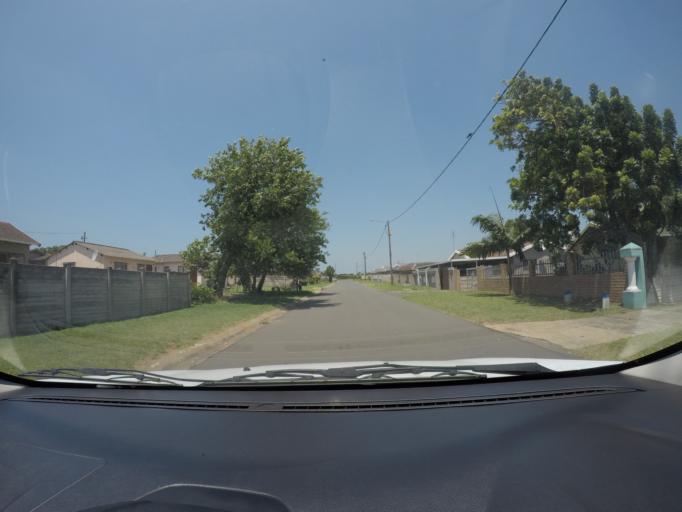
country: ZA
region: KwaZulu-Natal
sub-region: uThungulu District Municipality
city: eSikhawini
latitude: -28.8703
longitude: 31.9129
